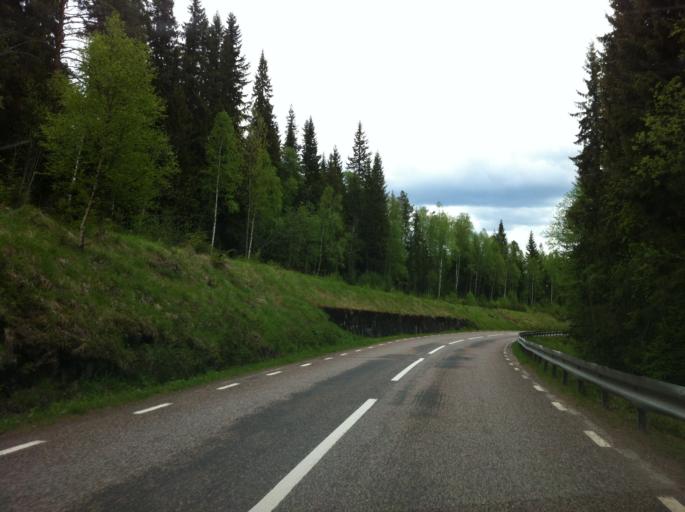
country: SE
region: Dalarna
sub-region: Malung-Saelens kommun
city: Malung
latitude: 61.2196
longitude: 13.2199
